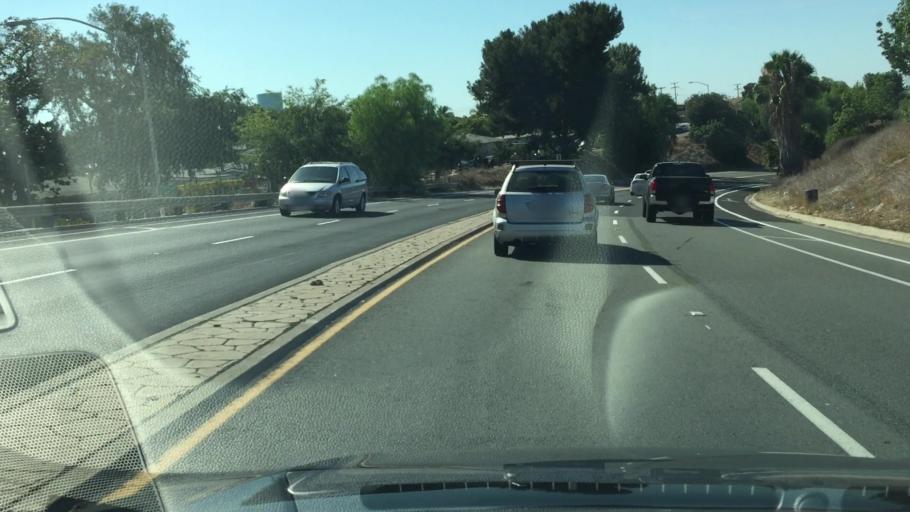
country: US
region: California
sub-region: San Diego County
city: Lemon Grove
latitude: 32.7465
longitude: -117.0610
